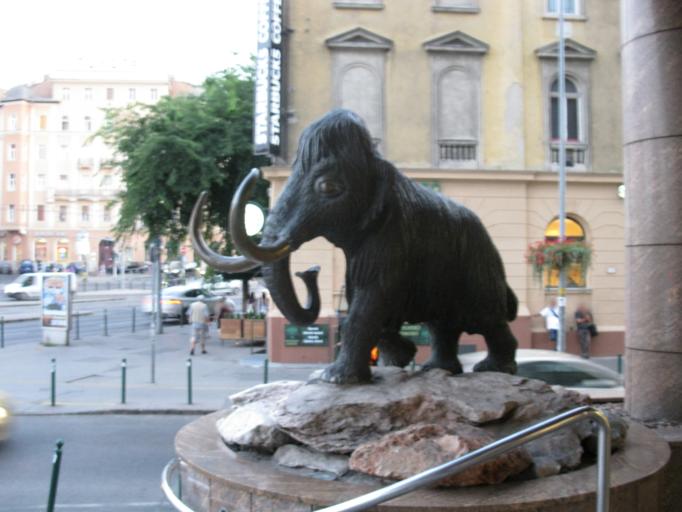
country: HU
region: Budapest
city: Budapest II. keruelet
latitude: 47.5082
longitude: 19.0266
